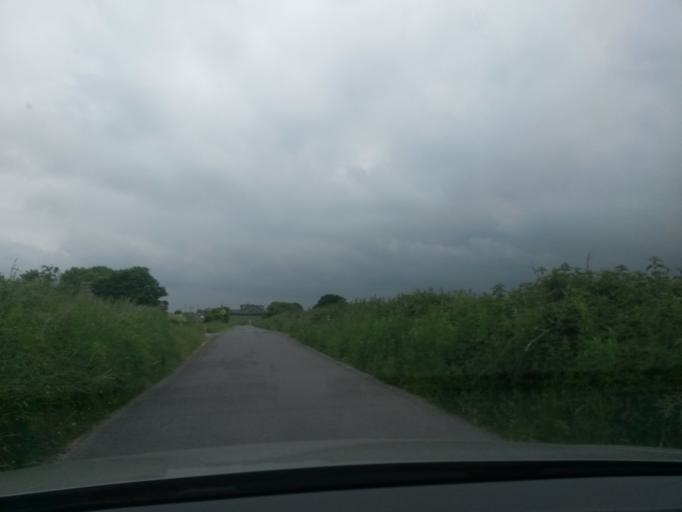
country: IE
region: Munster
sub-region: Ciarrai
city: Tralee
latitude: 52.3373
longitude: -9.7865
